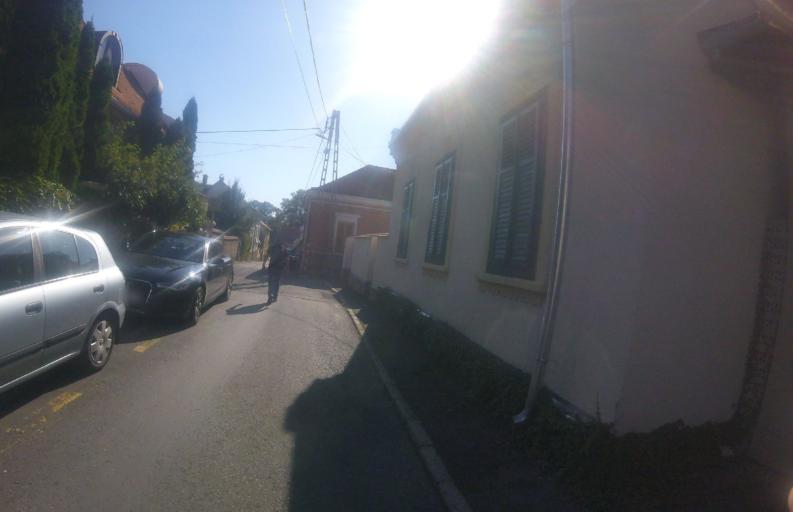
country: HU
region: Zala
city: Keszthely
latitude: 46.7640
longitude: 17.2447
